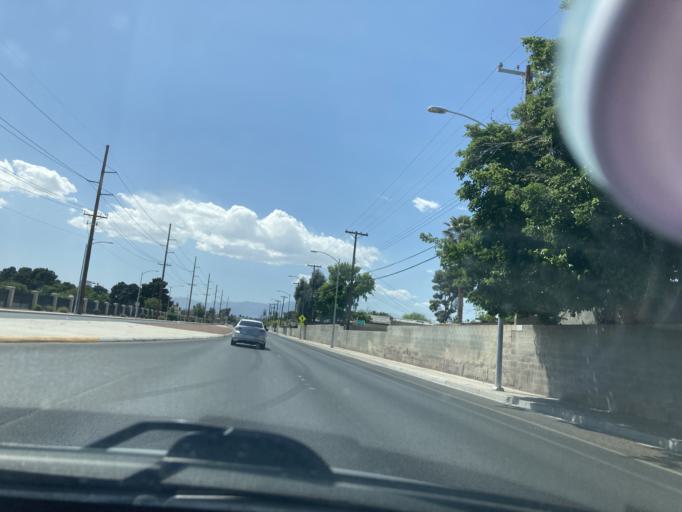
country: US
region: Nevada
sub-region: Clark County
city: North Las Vegas
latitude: 36.1811
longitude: -115.1031
